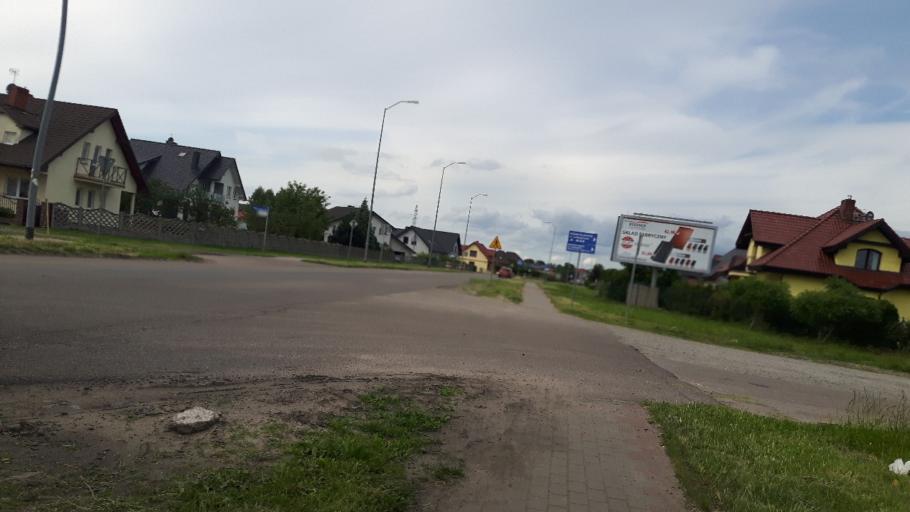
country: PL
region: West Pomeranian Voivodeship
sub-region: Powiat goleniowski
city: Goleniow
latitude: 53.4411
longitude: 14.7394
